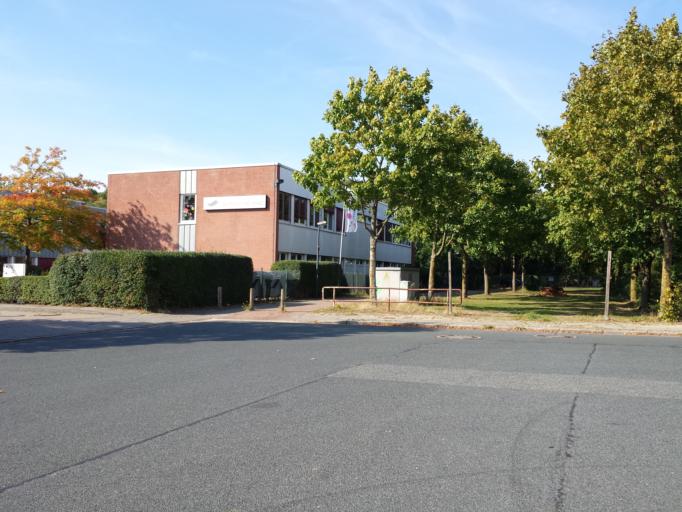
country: DE
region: Bremen
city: Bremen
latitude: 53.0498
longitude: 8.8351
